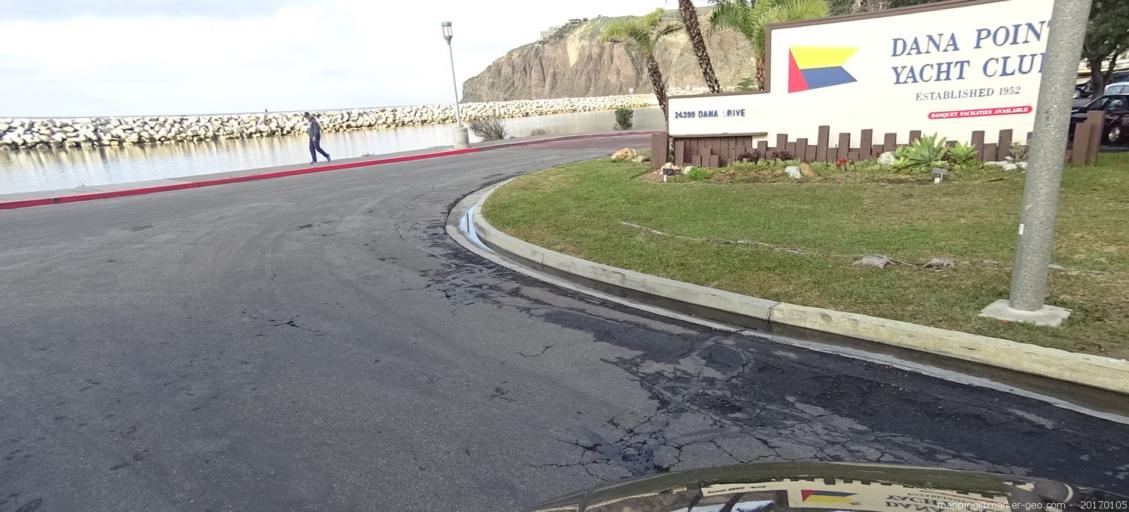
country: US
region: California
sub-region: Orange County
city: Dana Point
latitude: 33.4593
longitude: -117.7037
